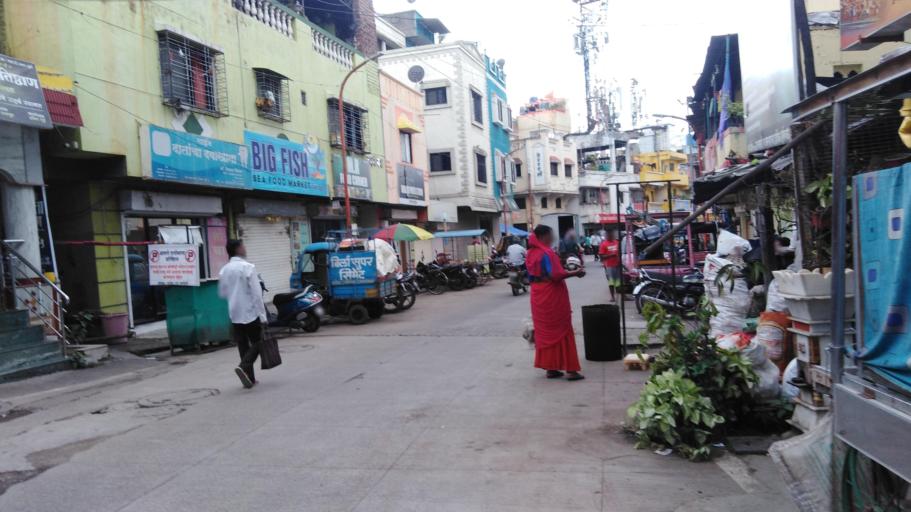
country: IN
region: Maharashtra
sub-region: Pune Division
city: Khadki
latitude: 18.5482
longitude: 73.8787
